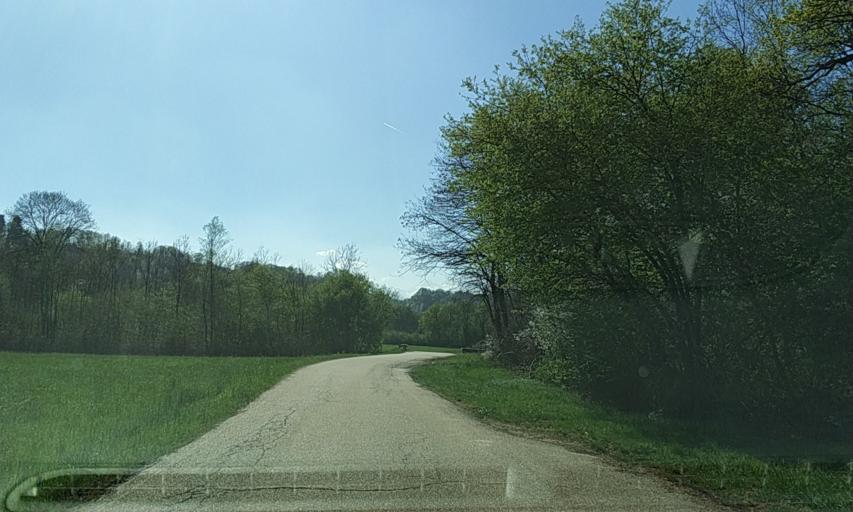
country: IT
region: Piedmont
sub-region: Provincia di Torino
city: Vauda Canavese Superiore
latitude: 45.2850
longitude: 7.6020
